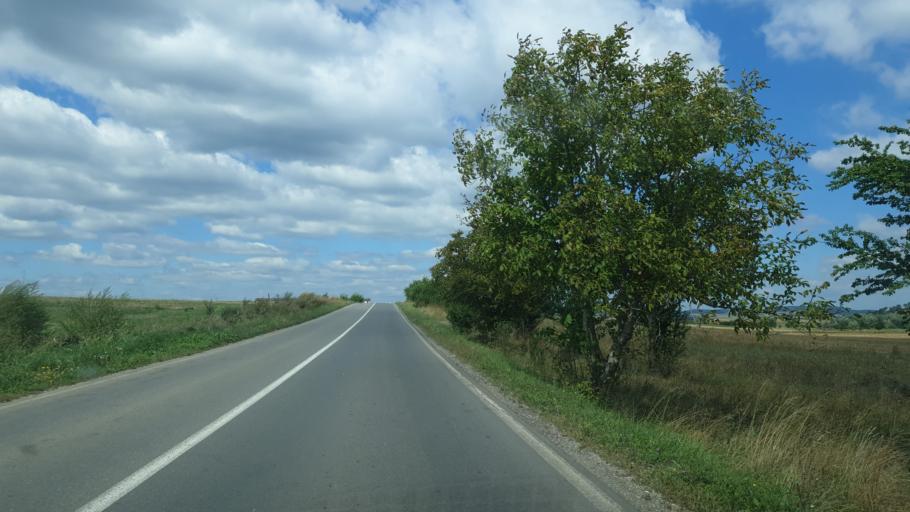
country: RO
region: Brasov
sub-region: Comuna Sanpetru
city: Sanpetru
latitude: 45.7231
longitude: 25.6278
